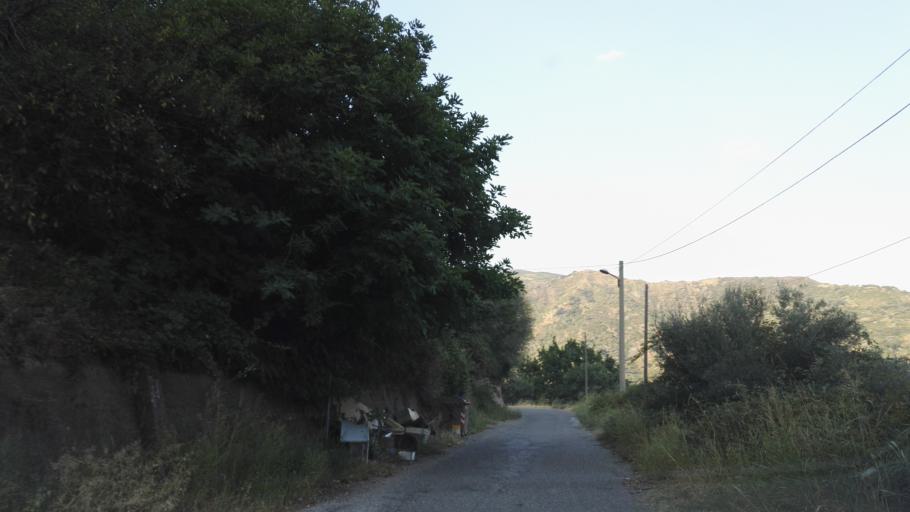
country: IT
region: Calabria
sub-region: Provincia di Reggio Calabria
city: Caulonia
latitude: 38.4115
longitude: 16.3691
